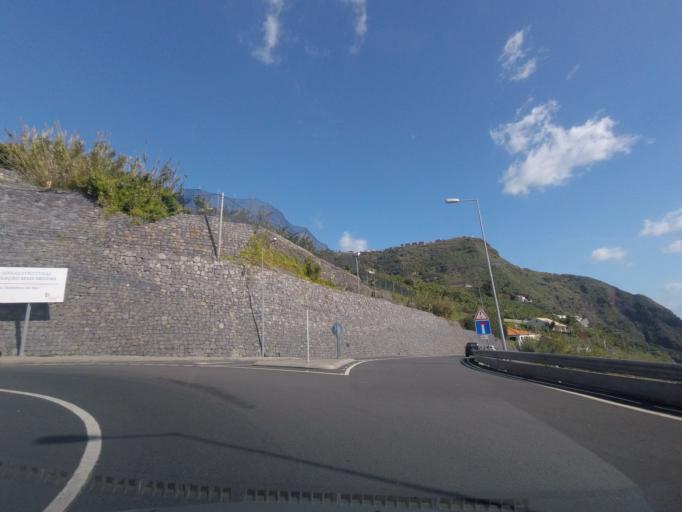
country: PT
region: Madeira
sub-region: Calheta
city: Arco da Calheta
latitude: 32.7114
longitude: -17.1524
